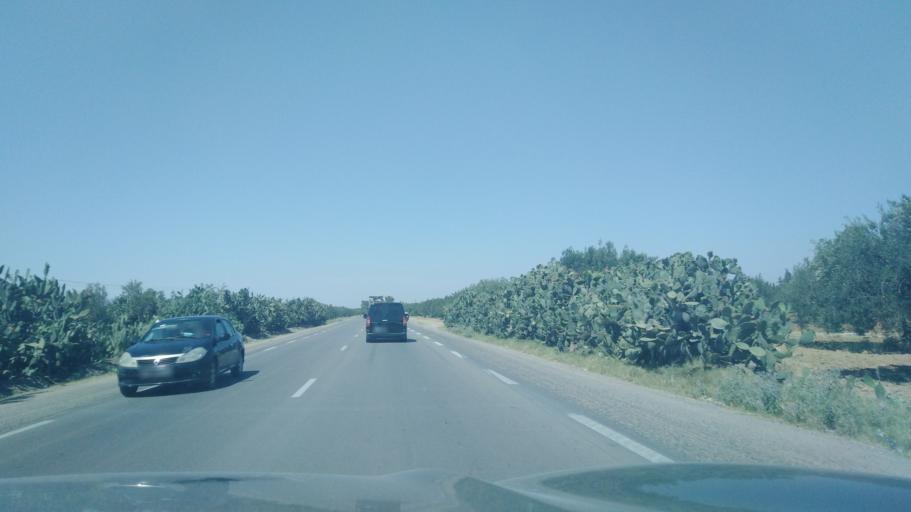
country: TN
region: Al Qayrawan
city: Kairouan
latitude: 35.6115
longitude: 9.9154
